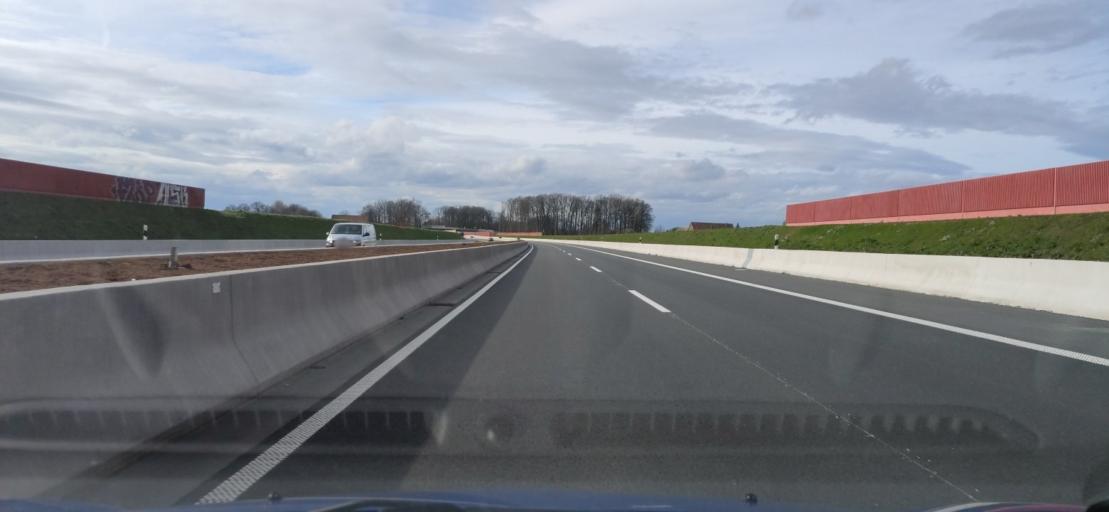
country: DE
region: North Rhine-Westphalia
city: Borgholzhausen
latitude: 52.0675
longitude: 8.3023
